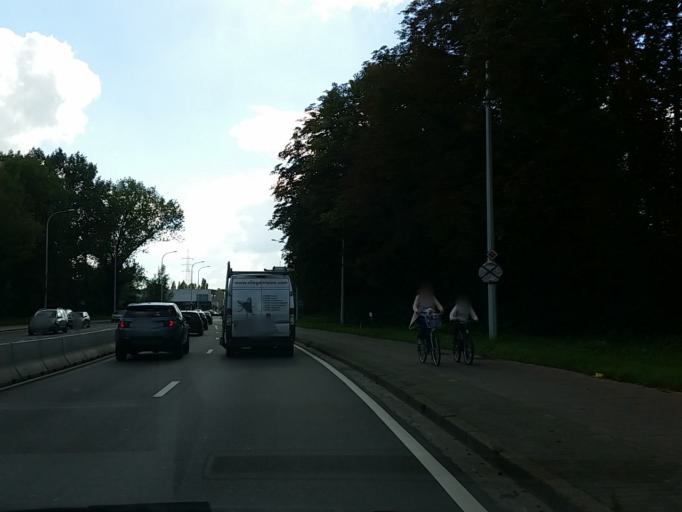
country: BE
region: Flanders
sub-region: Provincie Antwerpen
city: Borsbeek
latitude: 51.2172
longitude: 4.4957
